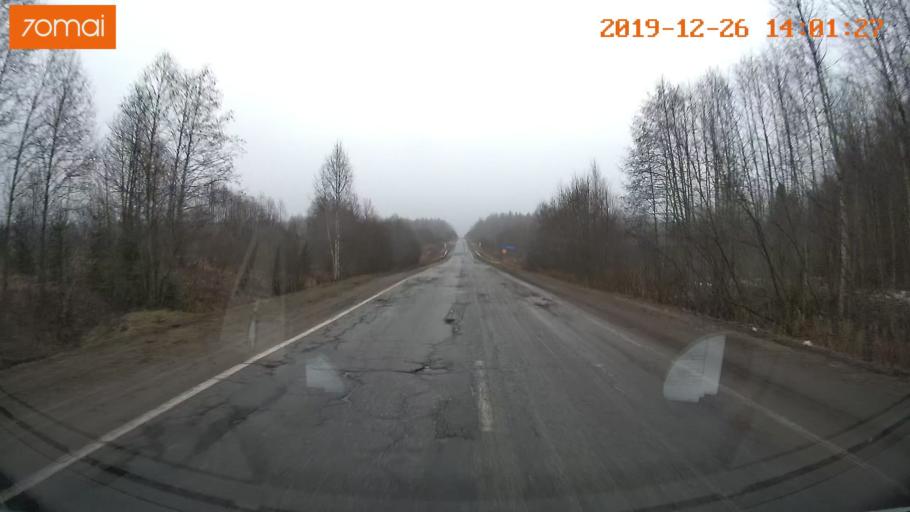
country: RU
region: Jaroslavl
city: Poshekhon'ye
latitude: 58.5504
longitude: 38.7641
